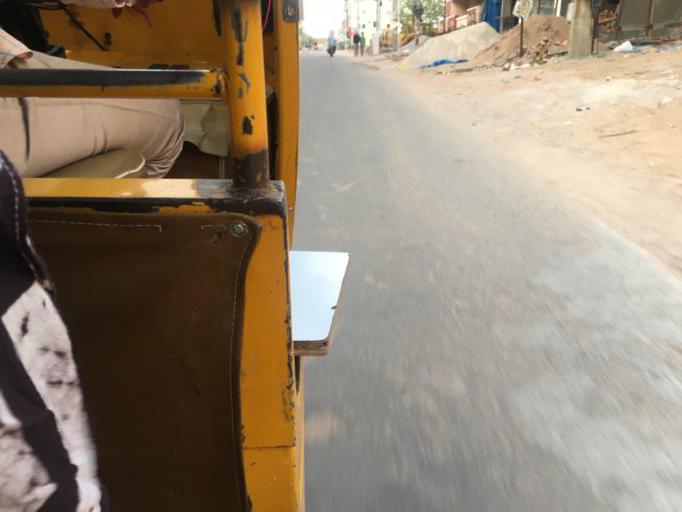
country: IN
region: Telangana
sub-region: Medak
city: Serilingampalle
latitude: 17.4321
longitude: 78.3339
